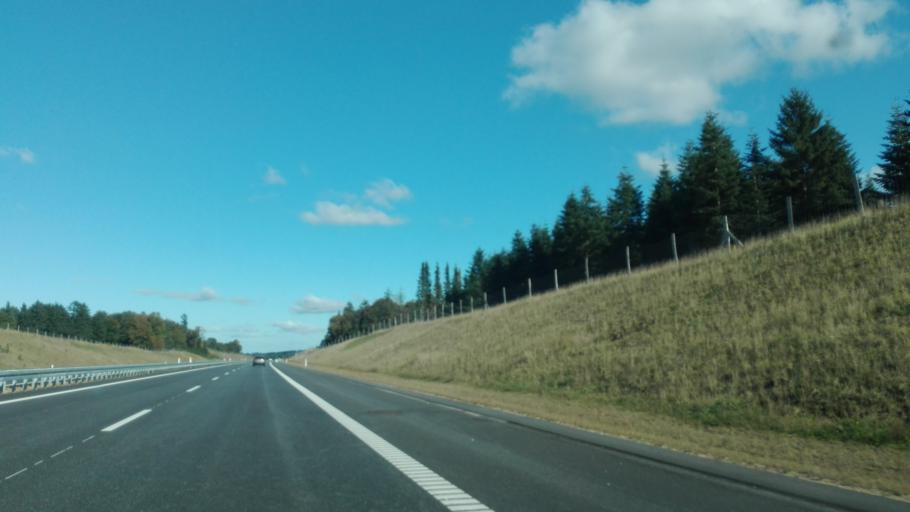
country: DK
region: Central Jutland
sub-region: Silkeborg Kommune
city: Silkeborg
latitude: 56.1726
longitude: 9.4755
